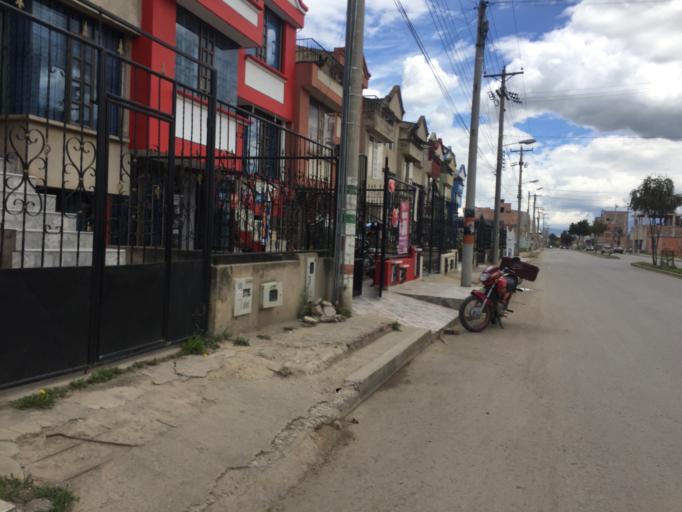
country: CO
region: Boyaca
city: Sogamoso
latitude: 5.7081
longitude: -72.9370
